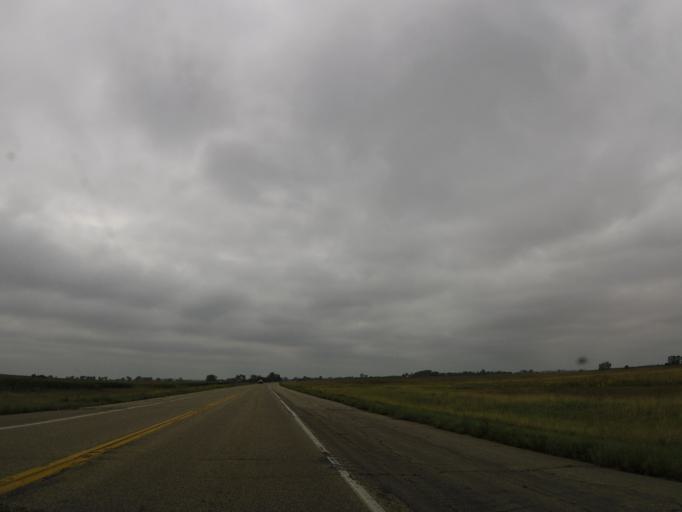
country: US
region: South Dakota
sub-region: Deuel County
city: Clear Lake
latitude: 44.9331
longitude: -96.6425
